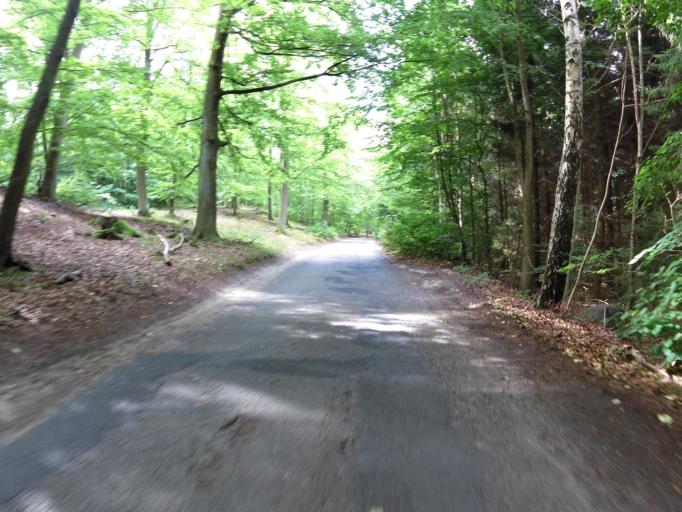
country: DE
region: Mecklenburg-Vorpommern
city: Seebad Bansin
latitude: 53.9856
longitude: 14.1101
